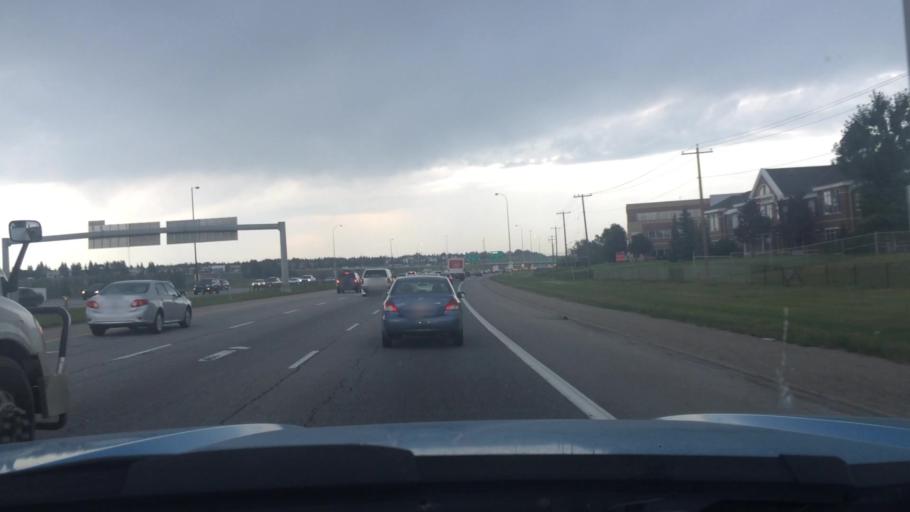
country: CA
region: Alberta
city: Calgary
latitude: 51.1029
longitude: -114.0449
